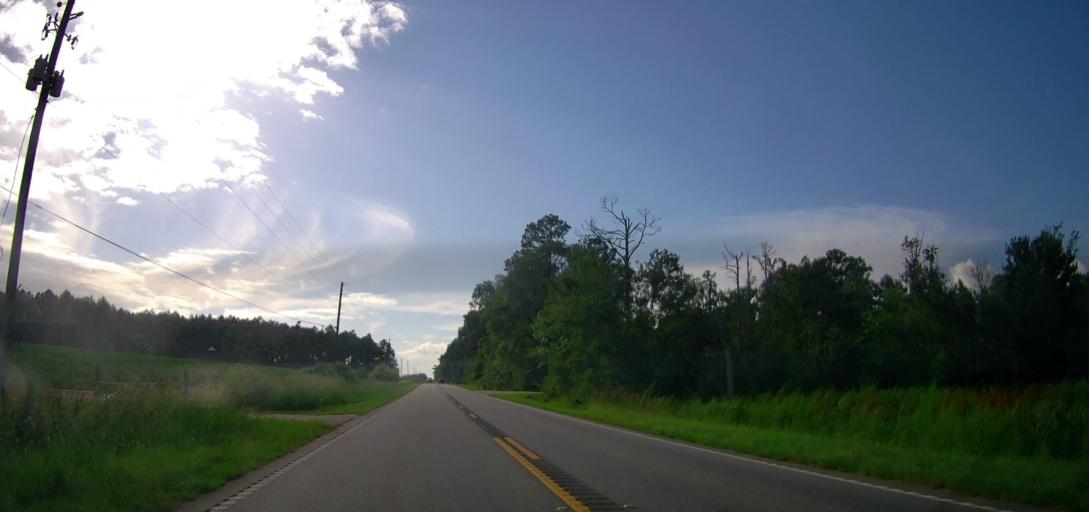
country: US
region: Georgia
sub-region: Coffee County
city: Douglas
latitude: 31.4786
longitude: -82.7899
